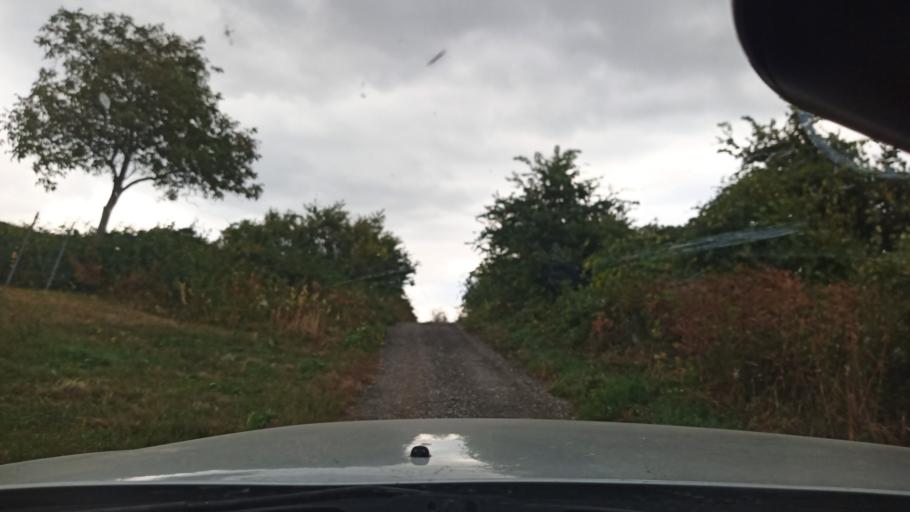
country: HU
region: Fejer
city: Bodajk
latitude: 47.3669
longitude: 18.2507
